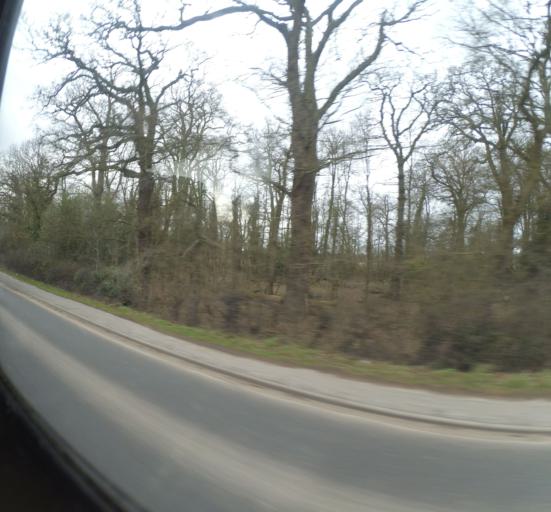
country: GB
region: England
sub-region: Warwickshire
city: Brandon
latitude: 52.4059
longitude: -1.4258
